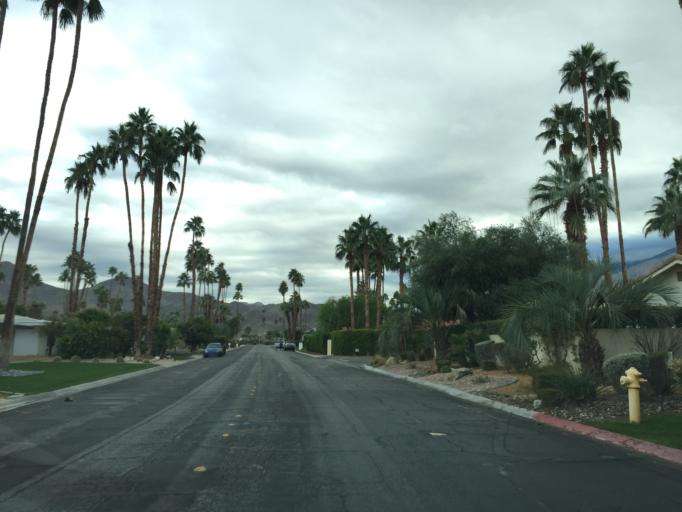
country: US
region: California
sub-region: Riverside County
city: Palm Springs
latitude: 33.7836
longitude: -116.5389
